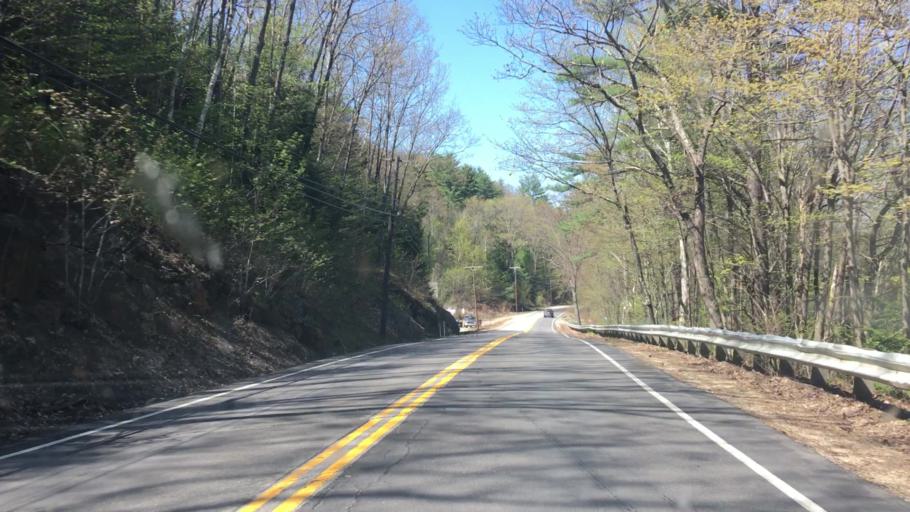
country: US
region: New Hampshire
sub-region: Grafton County
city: Plymouth
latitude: 43.7348
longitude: -71.6762
